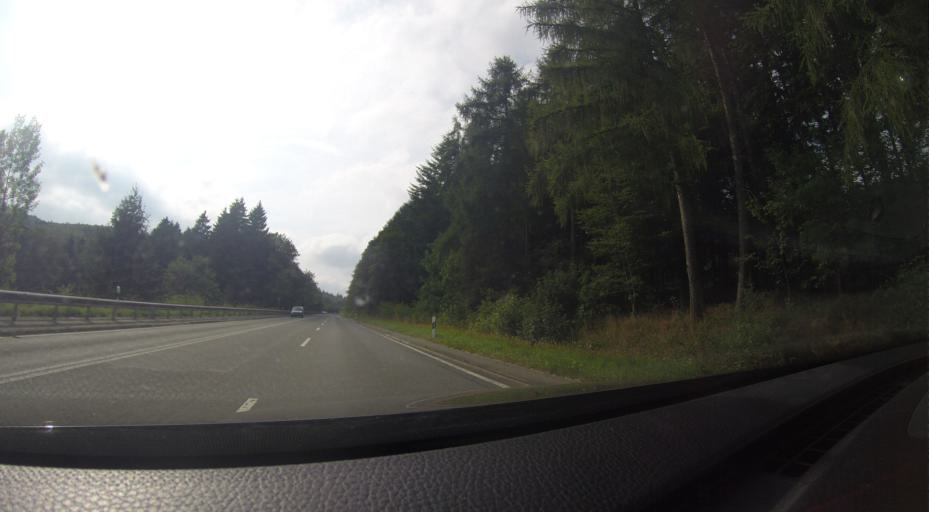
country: DE
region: Hesse
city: Willingen
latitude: 51.2151
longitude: 8.6255
